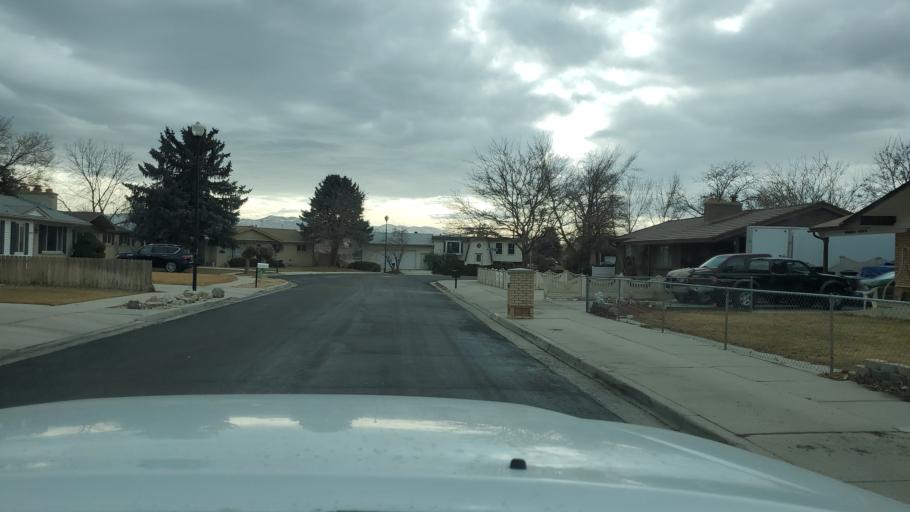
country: US
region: Utah
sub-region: Salt Lake County
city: White City
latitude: 40.5712
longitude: -111.8775
